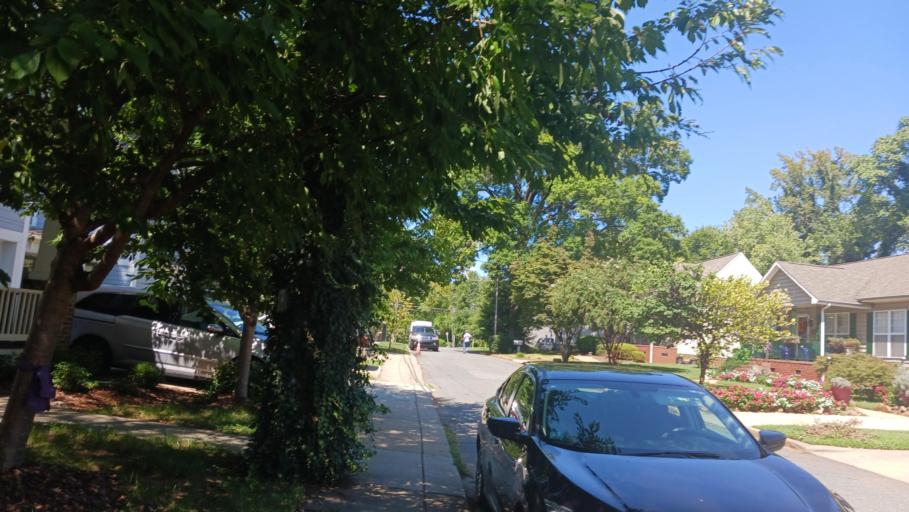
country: US
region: North Carolina
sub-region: Mecklenburg County
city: Charlotte
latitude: 35.2095
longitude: -80.8307
